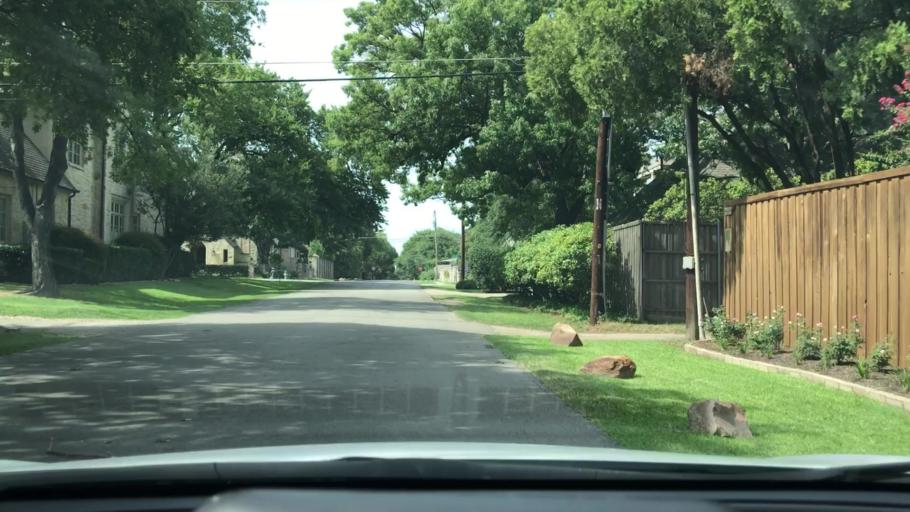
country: US
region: Texas
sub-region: Dallas County
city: University Park
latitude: 32.8846
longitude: -96.7900
